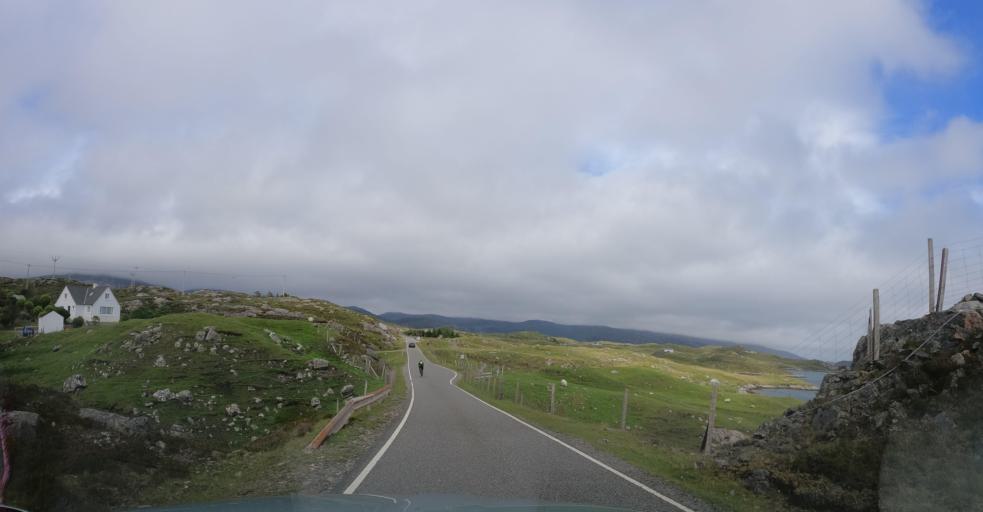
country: GB
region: Scotland
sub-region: Eilean Siar
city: Harris
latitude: 57.8819
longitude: -6.8154
